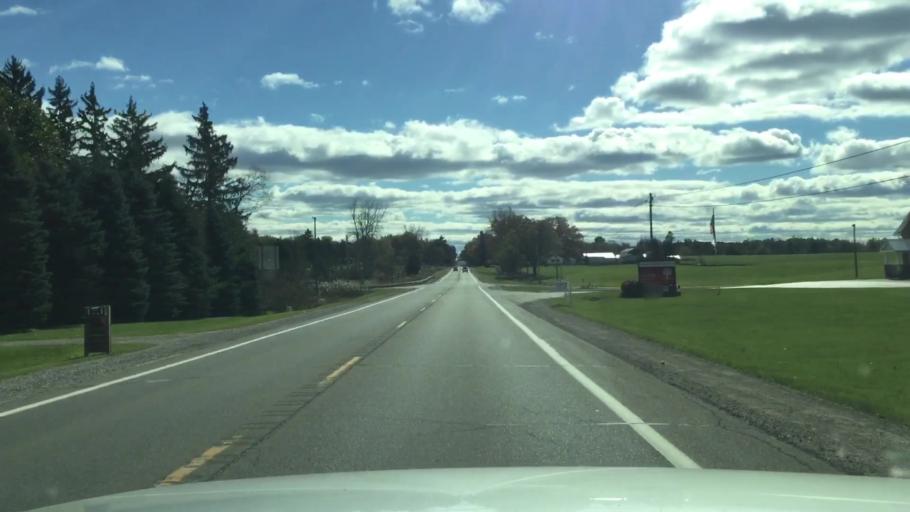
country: US
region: Michigan
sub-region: Lapeer County
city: Barnes Lake-Millers Lake
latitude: 43.1477
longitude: -83.3112
